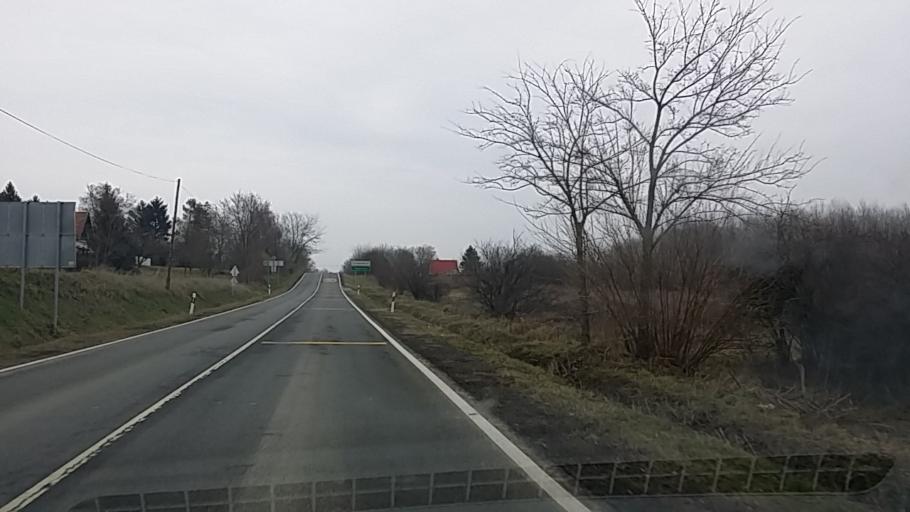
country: HU
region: Baranya
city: Dunaszekcso
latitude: 46.0664
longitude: 18.7452
